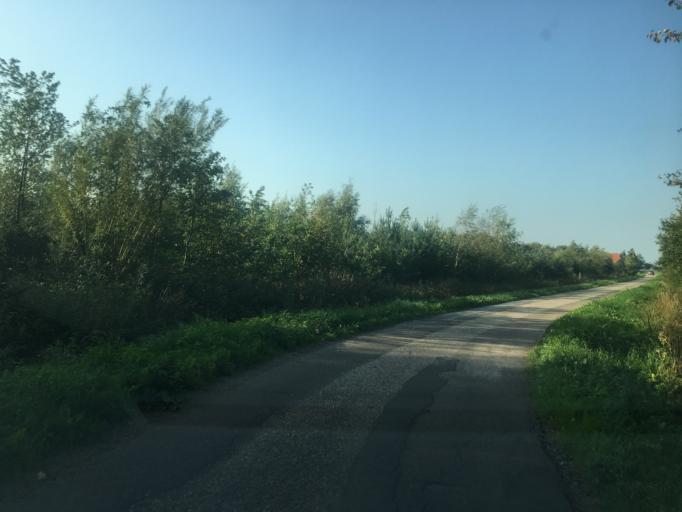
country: DE
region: Schleswig-Holstein
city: Ellhoft
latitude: 54.9294
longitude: 9.0030
